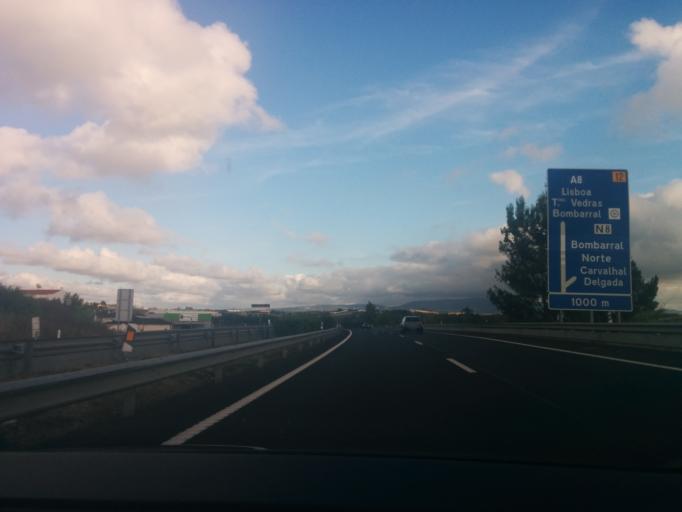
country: PT
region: Leiria
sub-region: Bombarral
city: Bombarral
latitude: 39.2968
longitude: -9.1614
